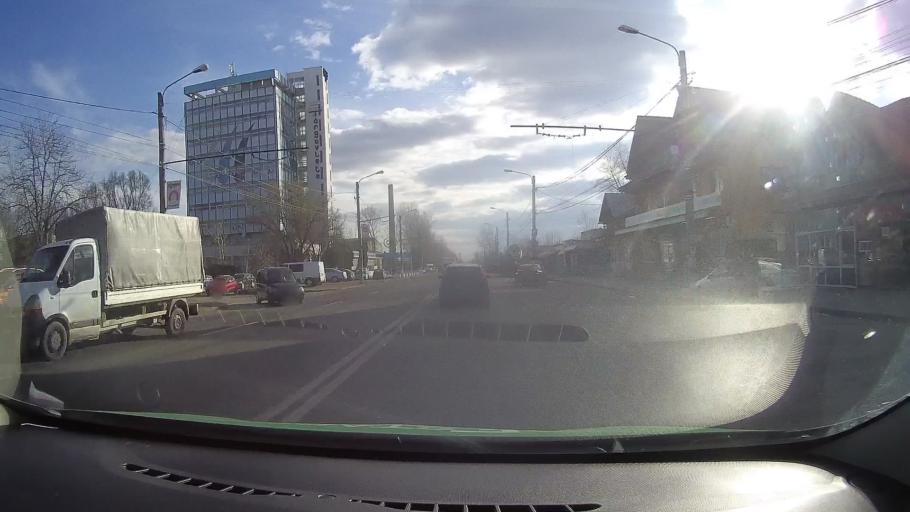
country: RO
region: Dambovita
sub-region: Comuna Lucieni
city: Lucieni
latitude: 44.8506
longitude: 25.4355
